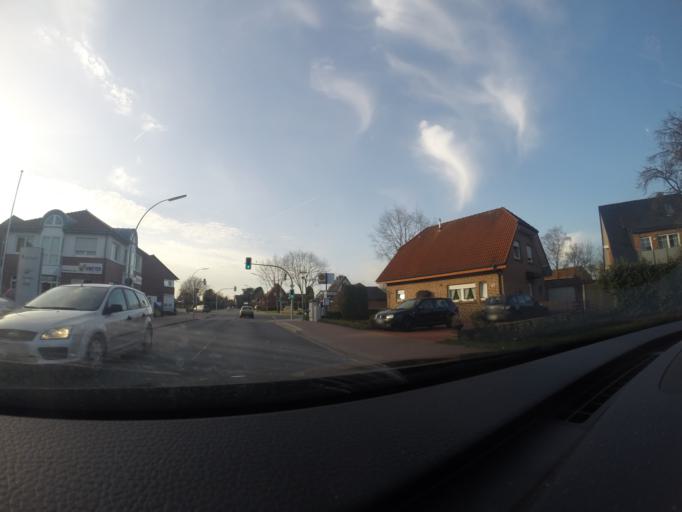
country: DE
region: North Rhine-Westphalia
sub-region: Regierungsbezirk Munster
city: Ahaus
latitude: 52.0923
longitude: 6.9762
